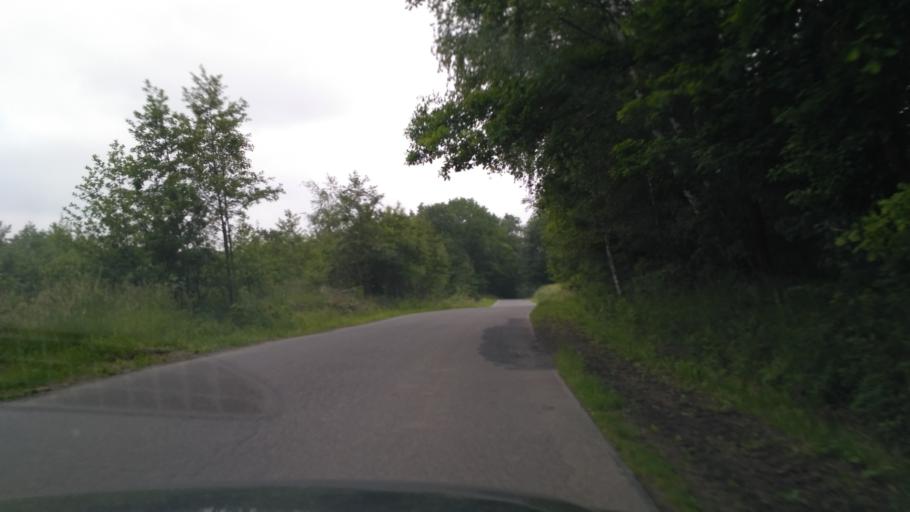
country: PL
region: Subcarpathian Voivodeship
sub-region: Powiat ropczycko-sedziszowski
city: Zagorzyce
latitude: 50.0100
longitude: 21.6772
